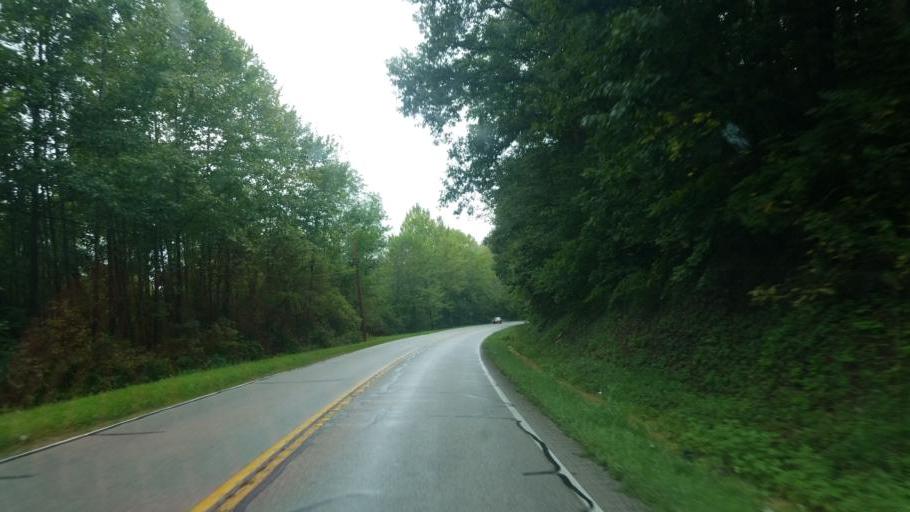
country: US
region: Kentucky
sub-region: Rowan County
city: Morehead
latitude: 38.1514
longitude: -83.4897
